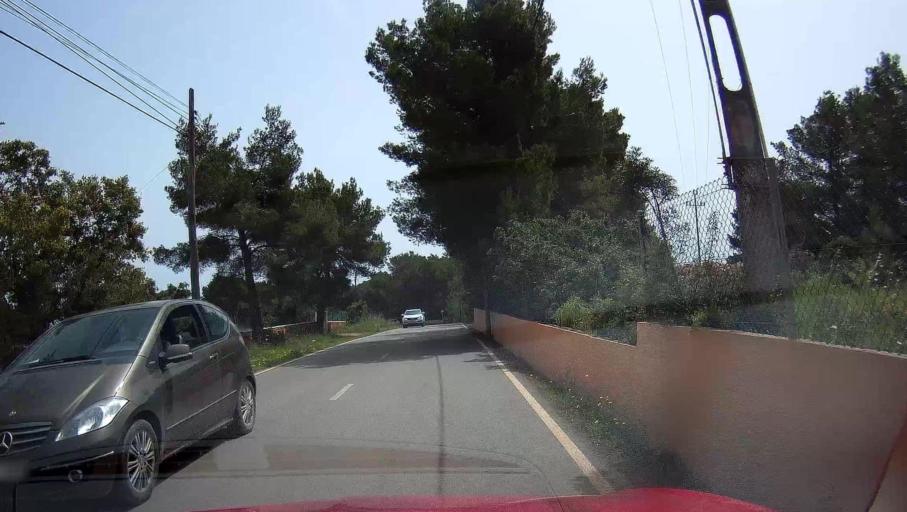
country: ES
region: Balearic Islands
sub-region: Illes Balears
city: Santa Eularia des Riu
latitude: 39.0108
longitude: 1.5665
